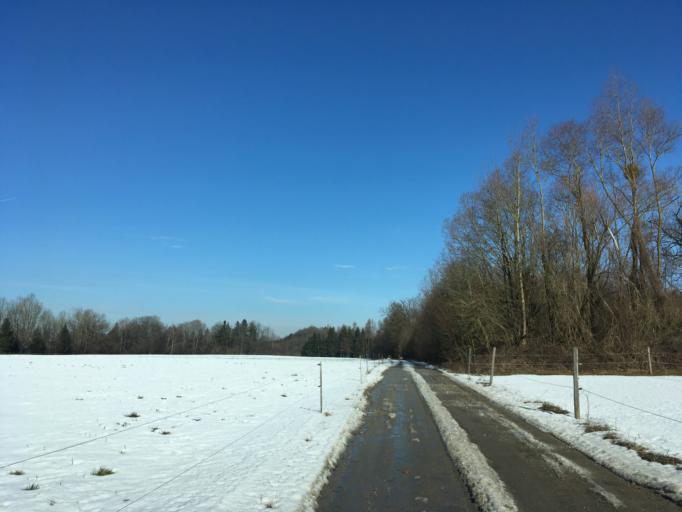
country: DE
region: Bavaria
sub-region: Upper Bavaria
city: Vogtareuth
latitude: 47.9627
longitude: 12.1616
